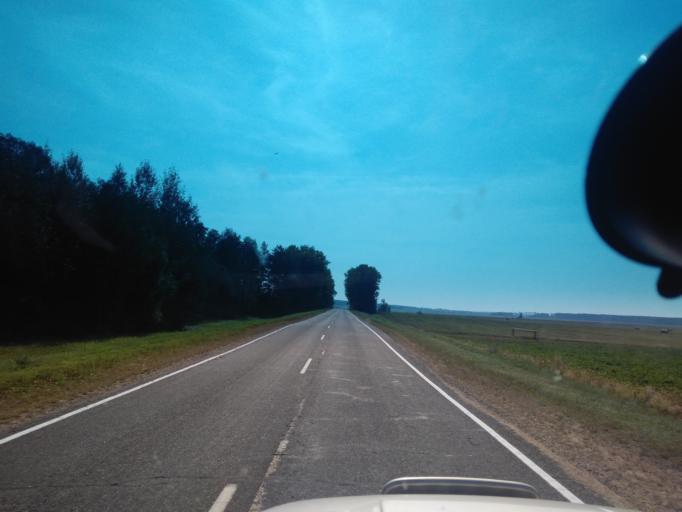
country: BY
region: Minsk
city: Uzda
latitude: 53.4062
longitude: 27.2226
